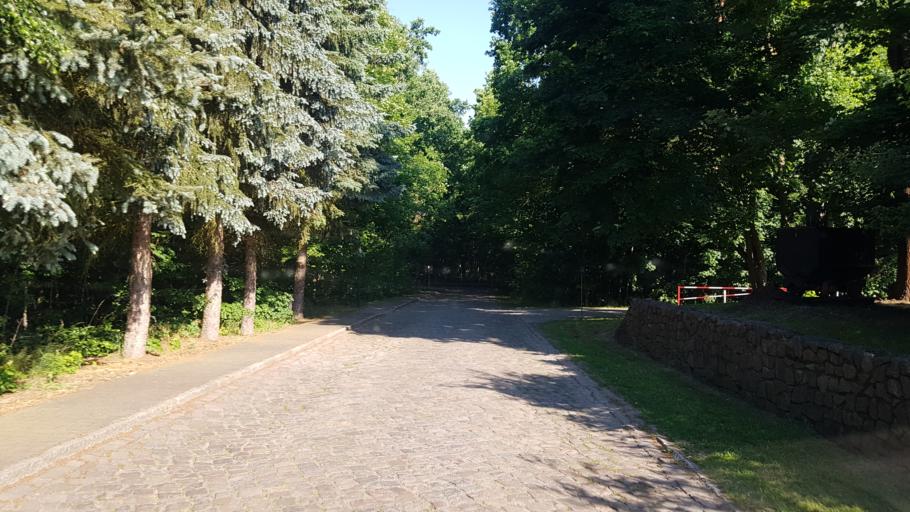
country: DE
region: Brandenburg
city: Lebusa
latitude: 51.7836
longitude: 13.3953
